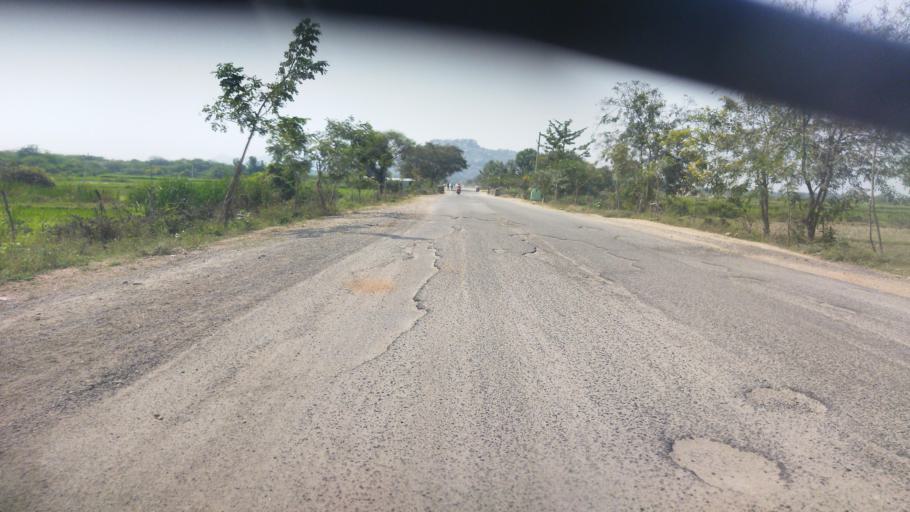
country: IN
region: Telangana
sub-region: Nalgonda
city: Nalgonda
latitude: 17.1161
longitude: 79.2829
